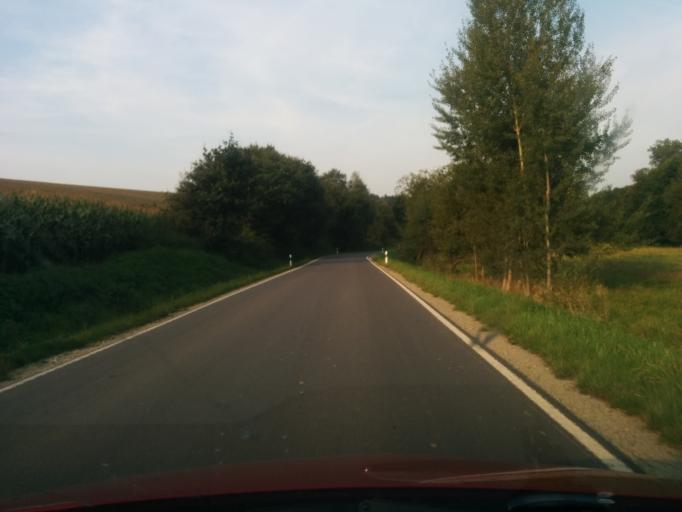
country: DE
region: Thuringia
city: Weissenborn-Luderode
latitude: 51.5605
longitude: 10.3866
